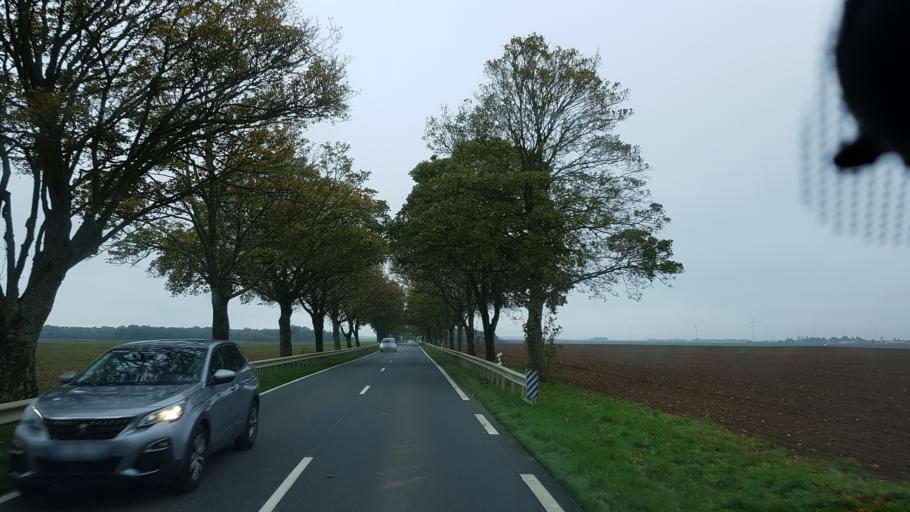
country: FR
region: Ile-de-France
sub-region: Departement de l'Essonne
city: Pussay
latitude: 48.4084
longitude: 1.9682
